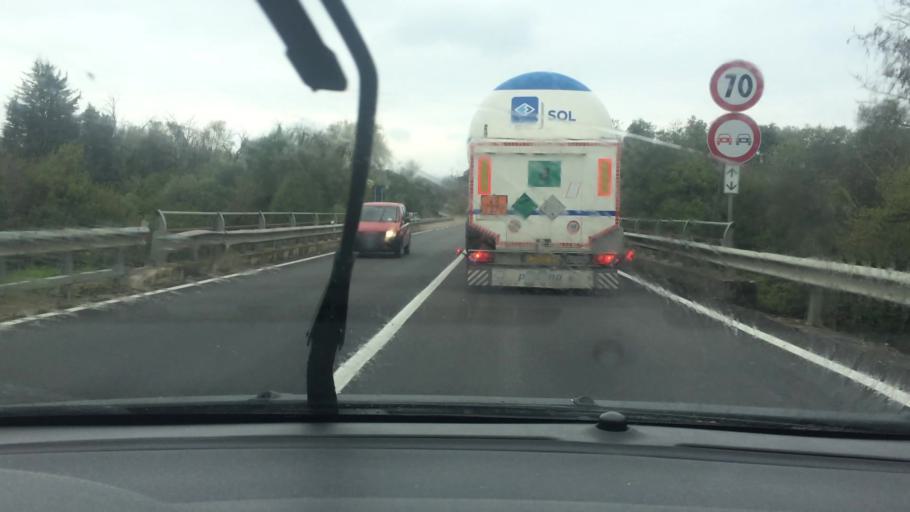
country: IT
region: Basilicate
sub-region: Provincia di Matera
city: Matera
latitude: 40.6124
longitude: 16.5754
